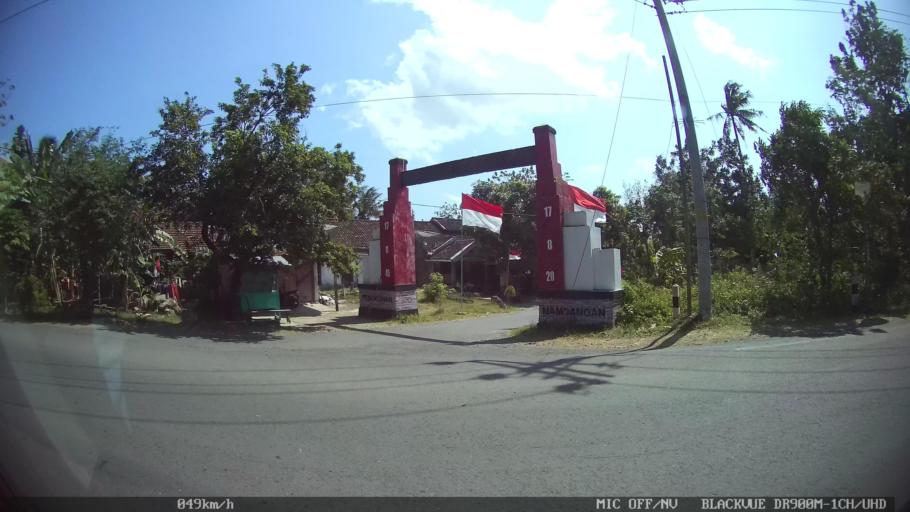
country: ID
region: Daerah Istimewa Yogyakarta
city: Pundong
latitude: -7.9631
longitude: 110.3555
